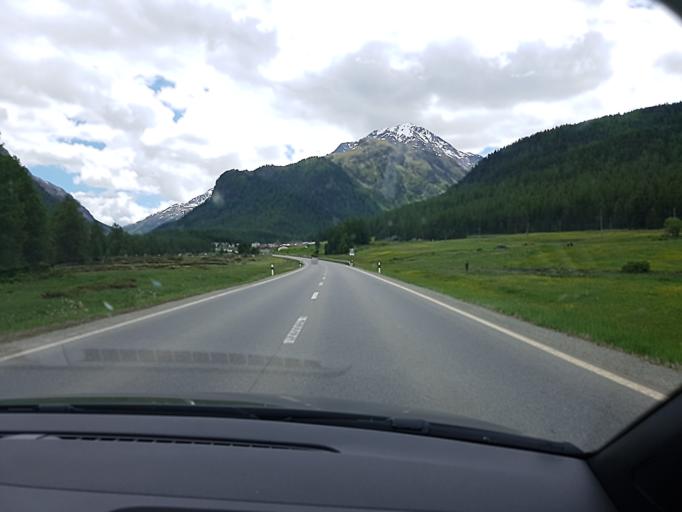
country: CH
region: Grisons
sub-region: Maloja District
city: Pontresina
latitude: 46.5009
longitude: 9.8888
